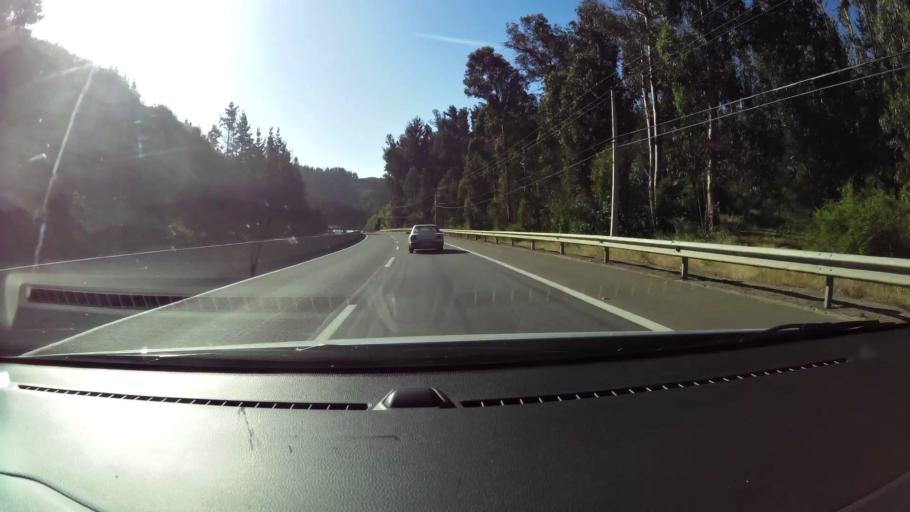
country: CL
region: Valparaiso
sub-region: Provincia de Valparaiso
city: Vina del Mar
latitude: -33.0892
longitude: -71.5550
